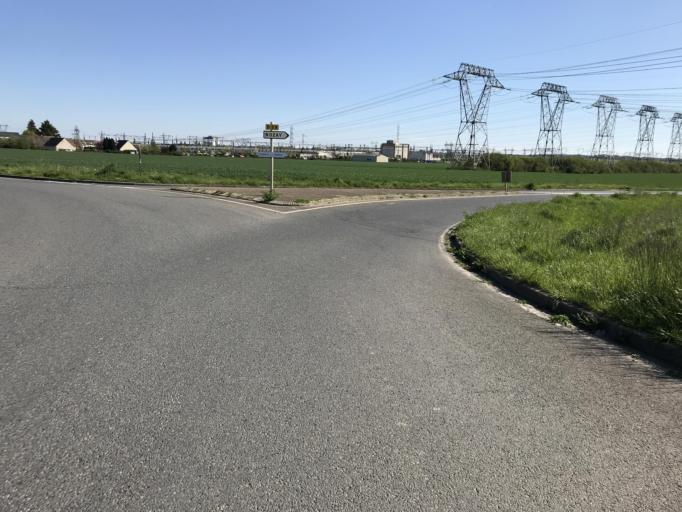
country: FR
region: Ile-de-France
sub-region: Departement de l'Essonne
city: Villejust
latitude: 48.6820
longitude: 2.2286
